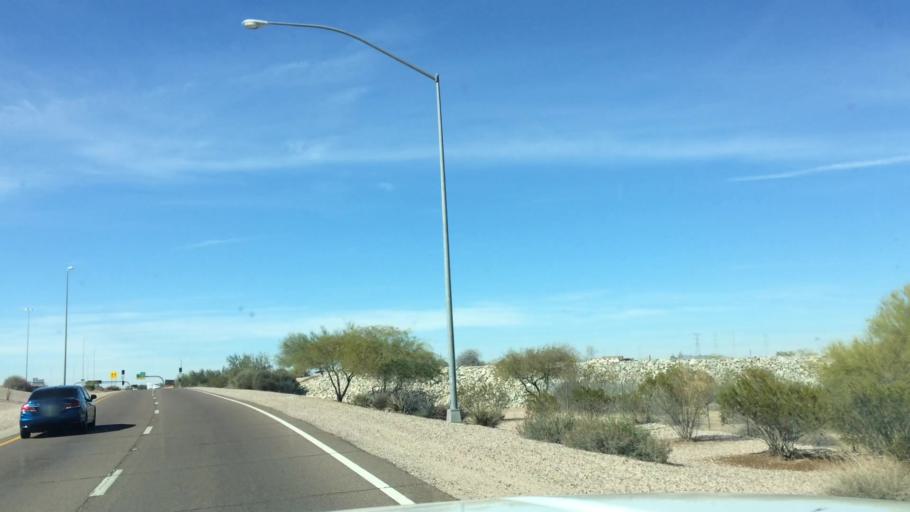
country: US
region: Arizona
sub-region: Maricopa County
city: Paradise Valley
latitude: 33.6483
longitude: -111.8935
